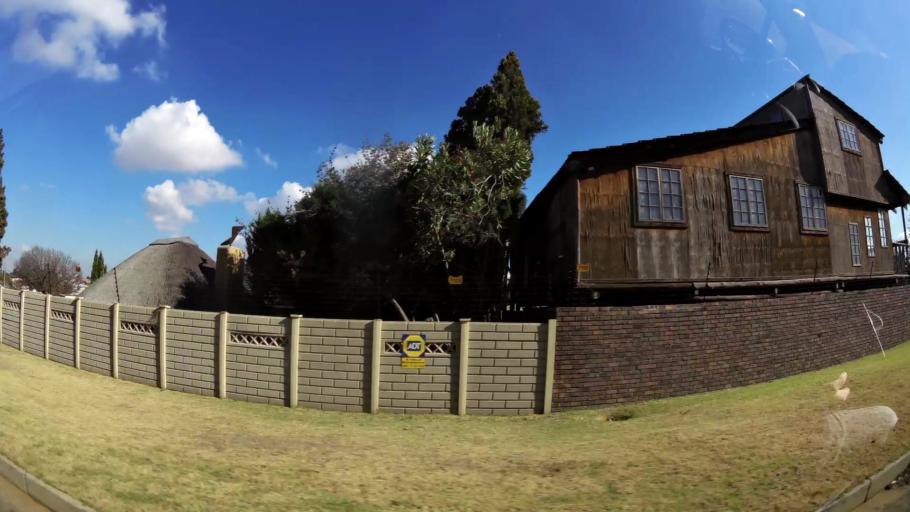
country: ZA
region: Gauteng
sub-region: City of Johannesburg Metropolitan Municipality
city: Roodepoort
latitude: -26.1421
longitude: 27.8224
